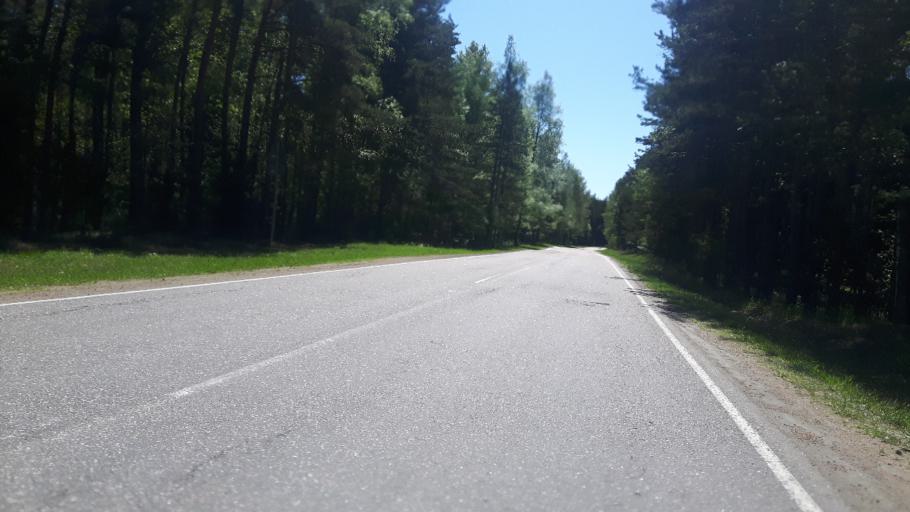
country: RU
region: Leningrad
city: Glebychevo
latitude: 60.3388
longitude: 28.8228
